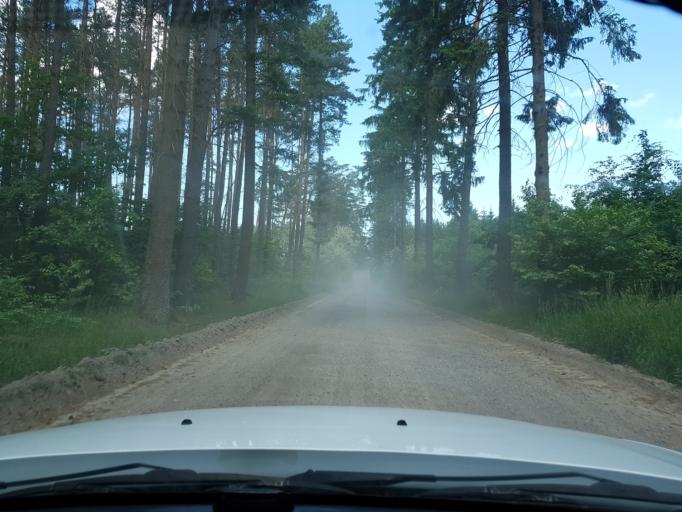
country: PL
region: West Pomeranian Voivodeship
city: Trzcinsko Zdroj
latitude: 52.8669
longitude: 14.5846
